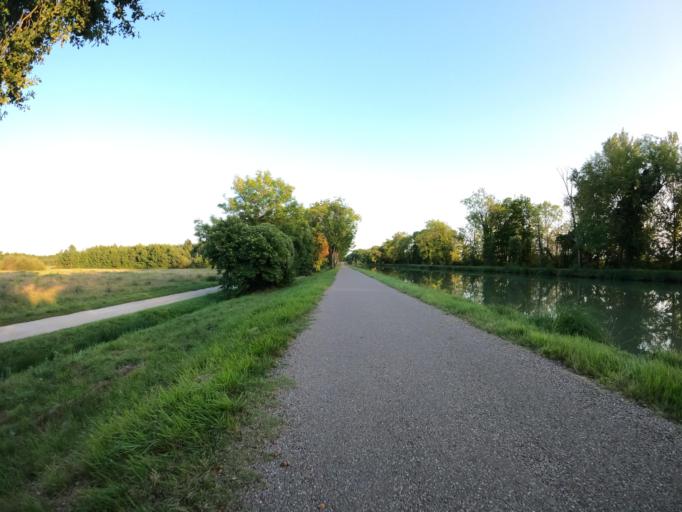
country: FR
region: Midi-Pyrenees
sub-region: Departement du Tarn-et-Garonne
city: Saint-Porquier
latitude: 43.9884
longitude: 1.2052
